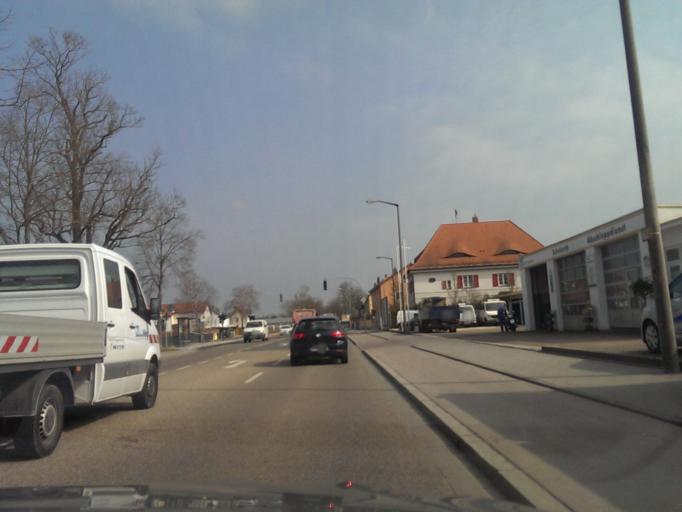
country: DE
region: Bavaria
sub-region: Upper Palatinate
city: Regensburg
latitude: 49.0253
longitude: 12.1443
